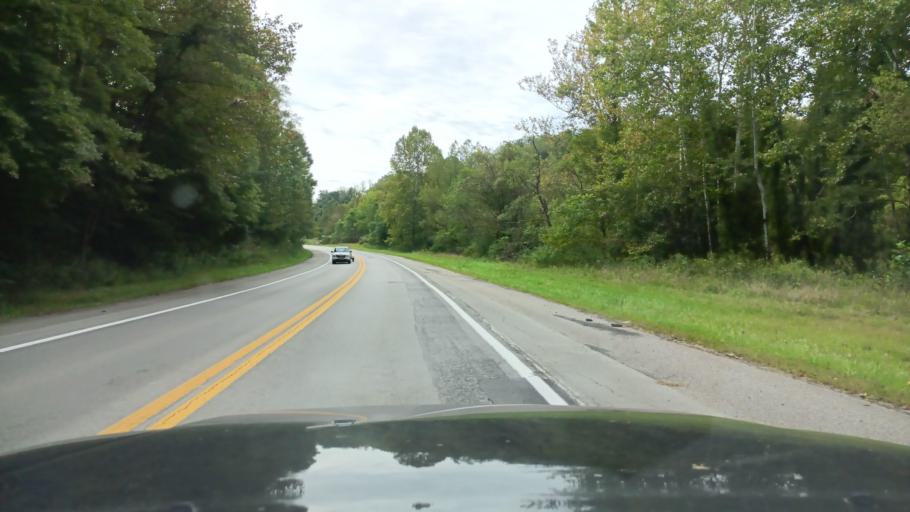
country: US
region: West Virginia
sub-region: Taylor County
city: Grafton
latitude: 39.3436
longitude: -80.0595
